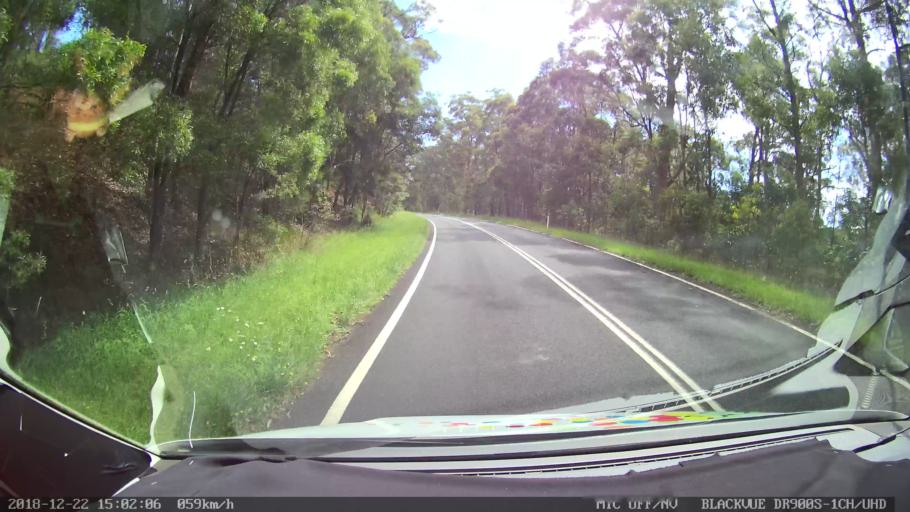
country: AU
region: New South Wales
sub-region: Bellingen
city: Dorrigo
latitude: -30.2596
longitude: 152.4538
